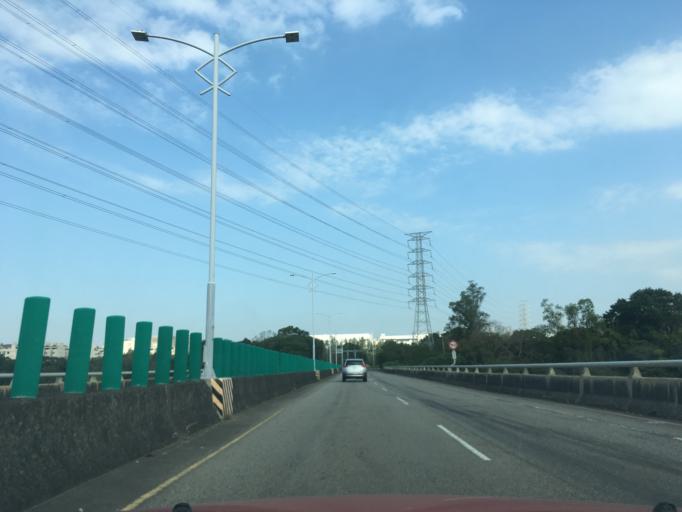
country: TW
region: Taiwan
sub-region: Hsinchu
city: Hsinchu
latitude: 24.7665
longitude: 121.0083
